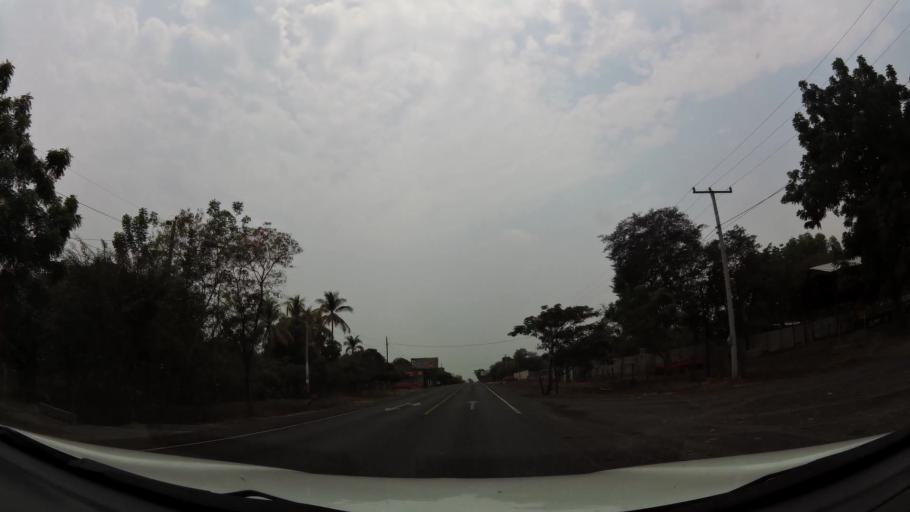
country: NI
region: Chinandega
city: Chichigalpa
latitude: 12.6046
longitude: -87.0551
